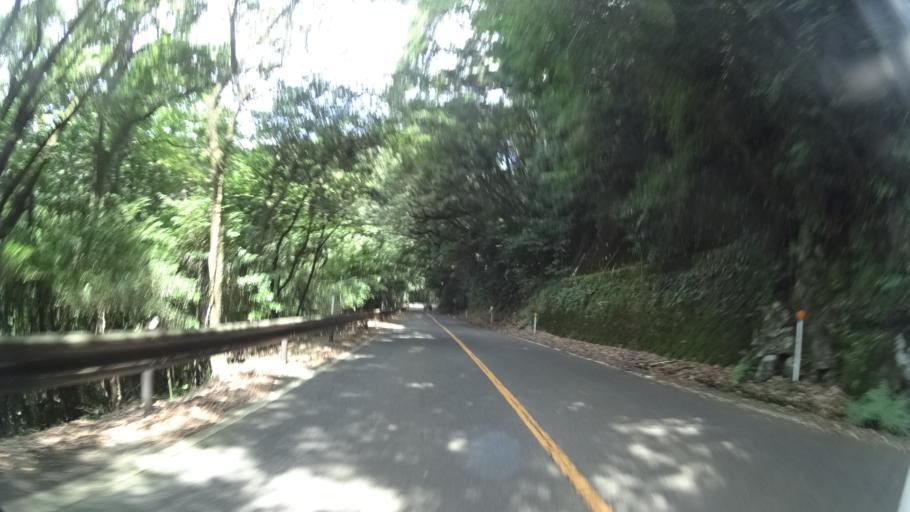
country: JP
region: Miyazaki
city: Kobayashi
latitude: 31.9018
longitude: 130.8392
